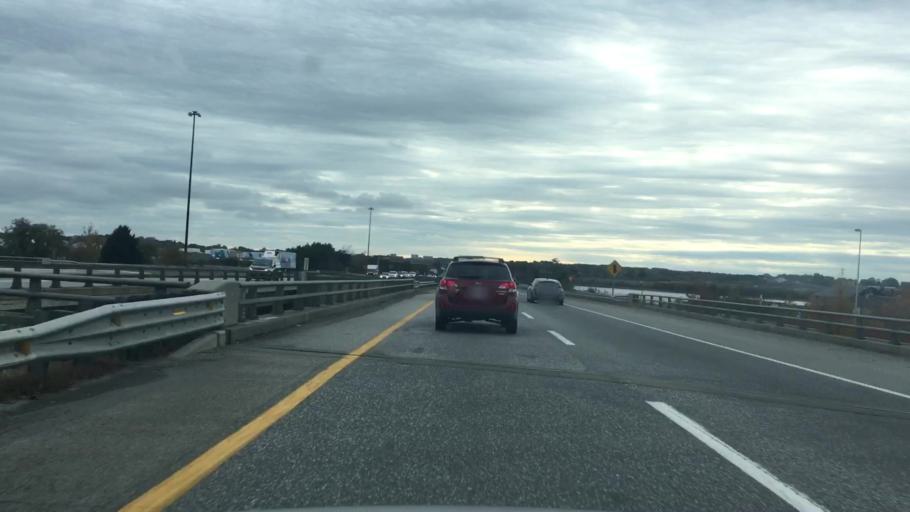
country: US
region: Maine
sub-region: Cumberland County
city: South Portland Gardens
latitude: 43.6535
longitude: -70.2876
